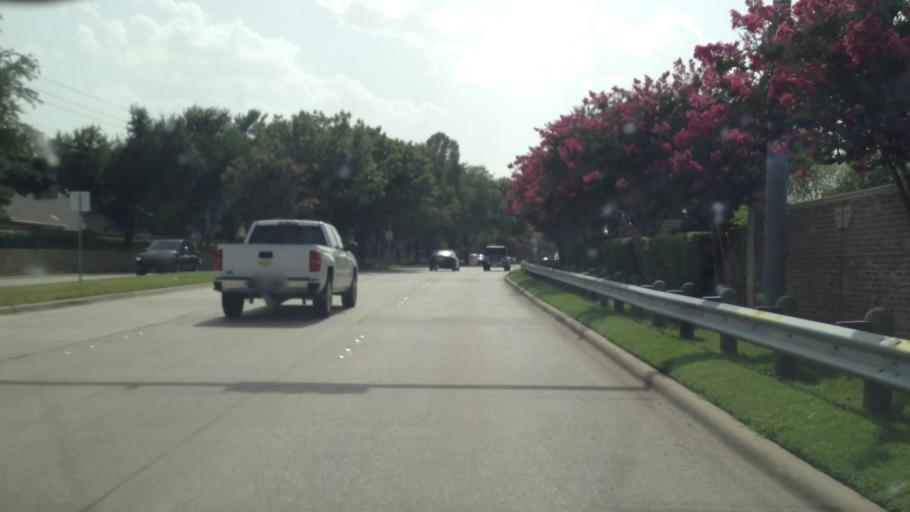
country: US
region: Texas
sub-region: Dallas County
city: Addison
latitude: 33.0277
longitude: -96.8191
